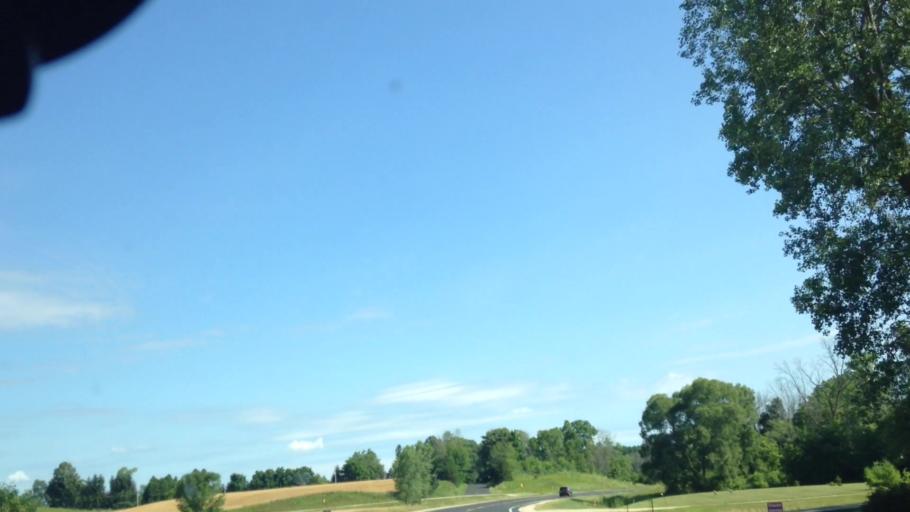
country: US
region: Wisconsin
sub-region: Washington County
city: Slinger
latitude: 43.3628
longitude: -88.2609
